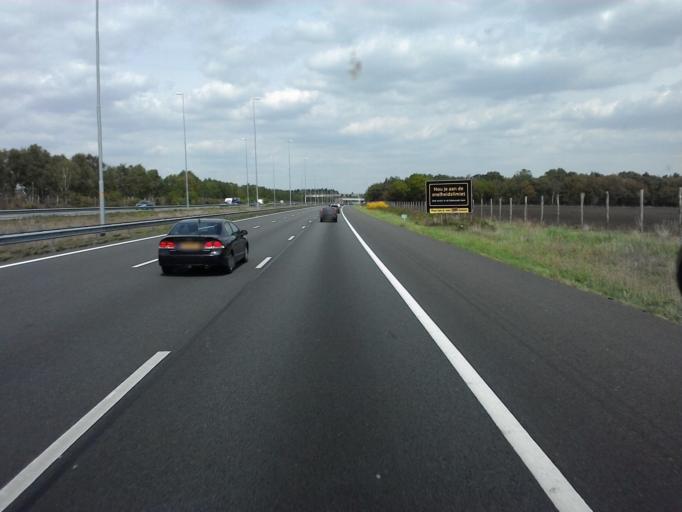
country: NL
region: Gelderland
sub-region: Gemeente Renkum
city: Heelsum
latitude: 51.9895
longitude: 5.7750
